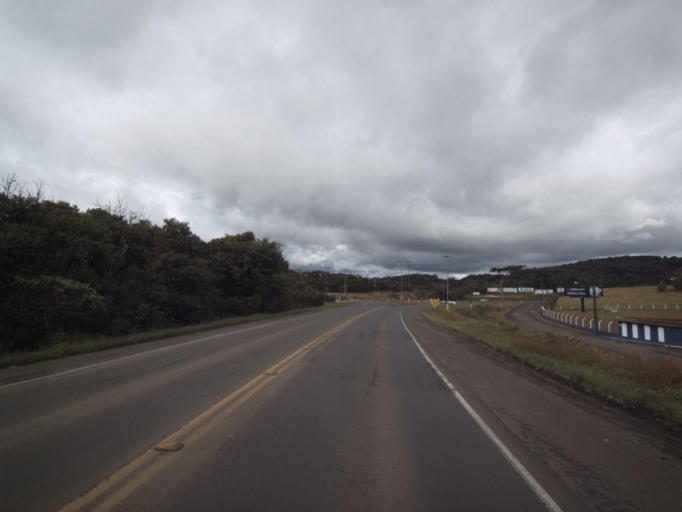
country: BR
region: Santa Catarina
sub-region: Concordia
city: Concordia
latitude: -27.2226
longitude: -51.9490
